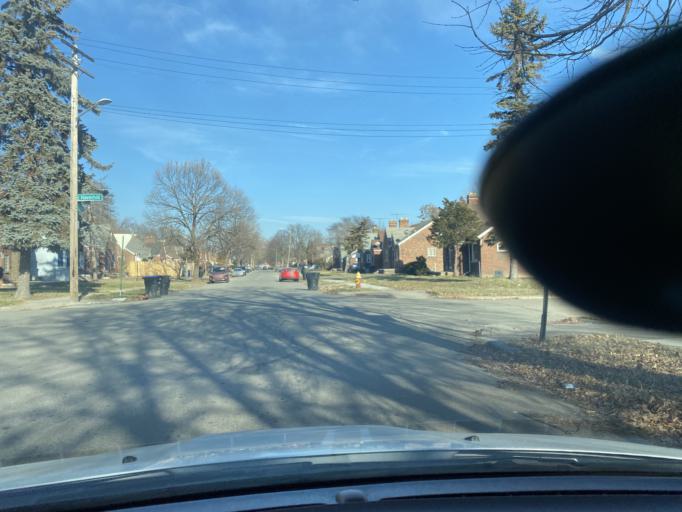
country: US
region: Michigan
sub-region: Wayne County
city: Harper Woods
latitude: 42.4115
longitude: -82.9523
